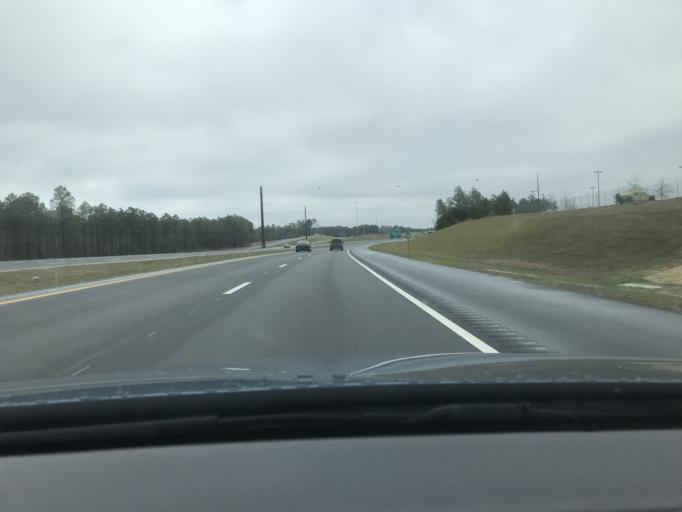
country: US
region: North Carolina
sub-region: Cumberland County
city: Fort Bragg
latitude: 35.1027
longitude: -79.0207
